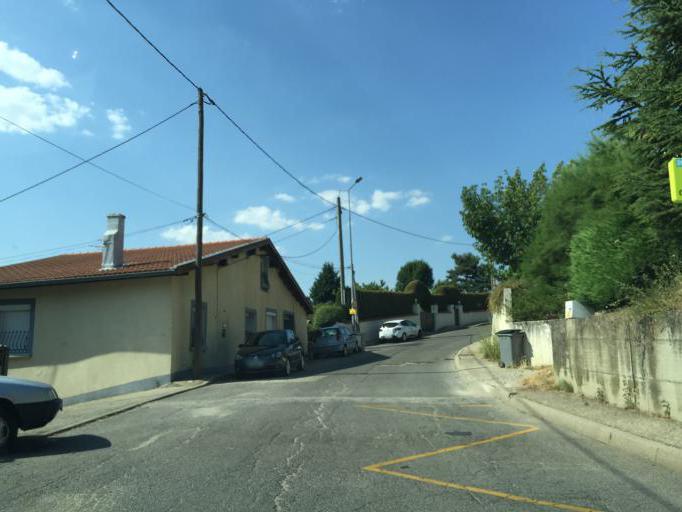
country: FR
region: Rhone-Alpes
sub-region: Departement de la Loire
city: Saint-Jean-Bonnefonds
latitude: 45.4270
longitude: 4.4386
